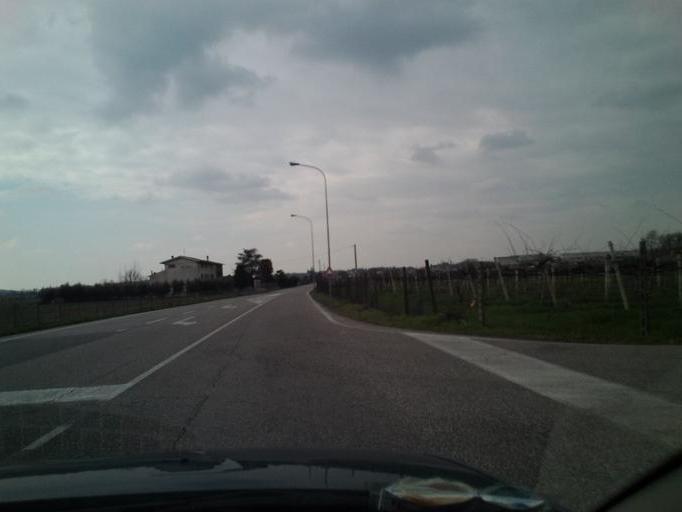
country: IT
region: Veneto
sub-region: Provincia di Verona
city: Caselle
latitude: 45.4090
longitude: 10.8776
